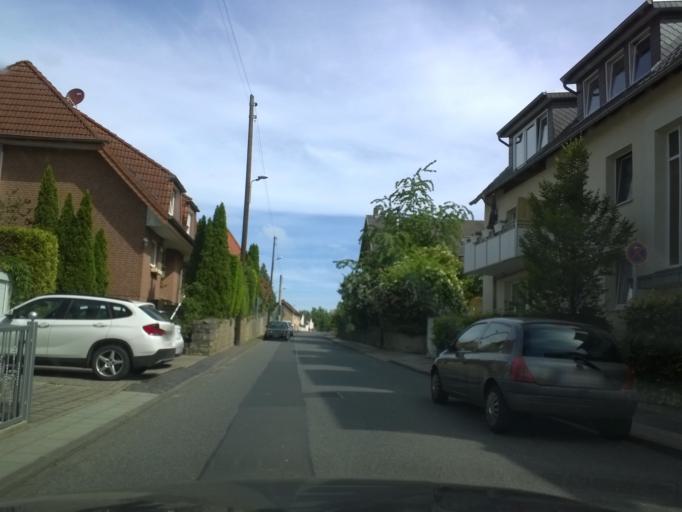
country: DE
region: Lower Saxony
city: Diekholzen
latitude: 52.1245
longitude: 9.9199
